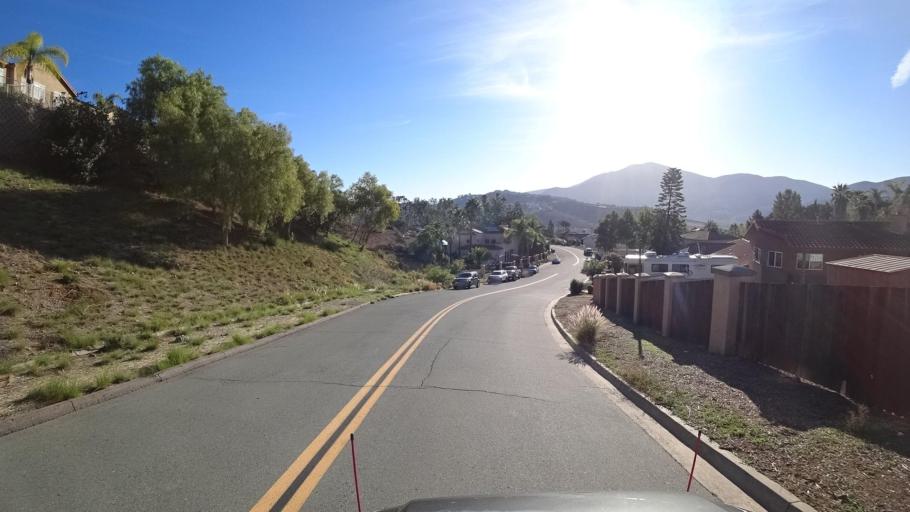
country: US
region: California
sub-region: San Diego County
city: La Presa
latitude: 32.7194
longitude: -116.9838
